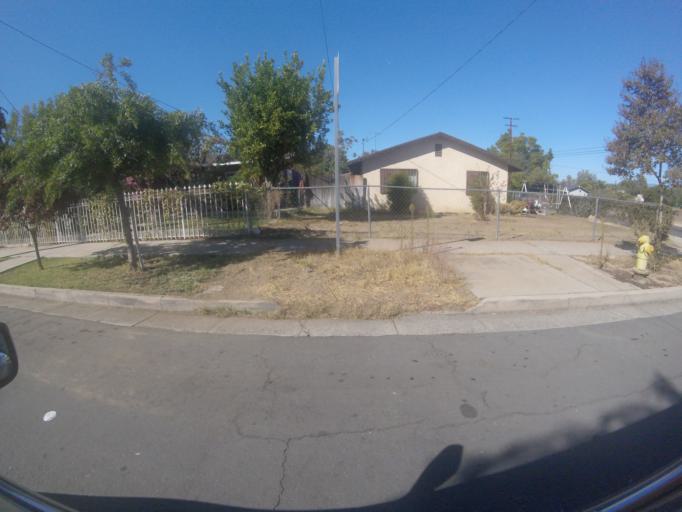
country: US
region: California
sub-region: San Bernardino County
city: Redlands
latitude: 34.0662
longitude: -117.1890
